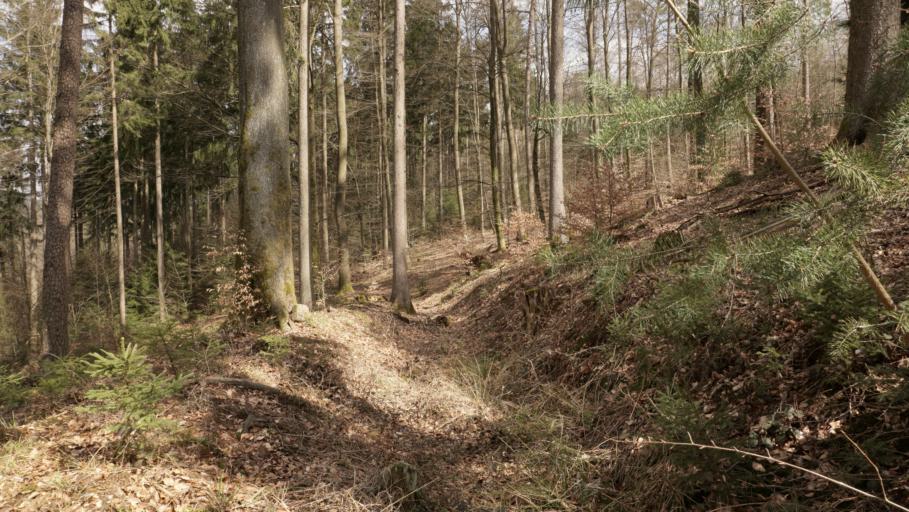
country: DE
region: Baden-Wuerttemberg
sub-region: Karlsruhe Region
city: Neckargerach
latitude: 49.4140
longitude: 9.1054
